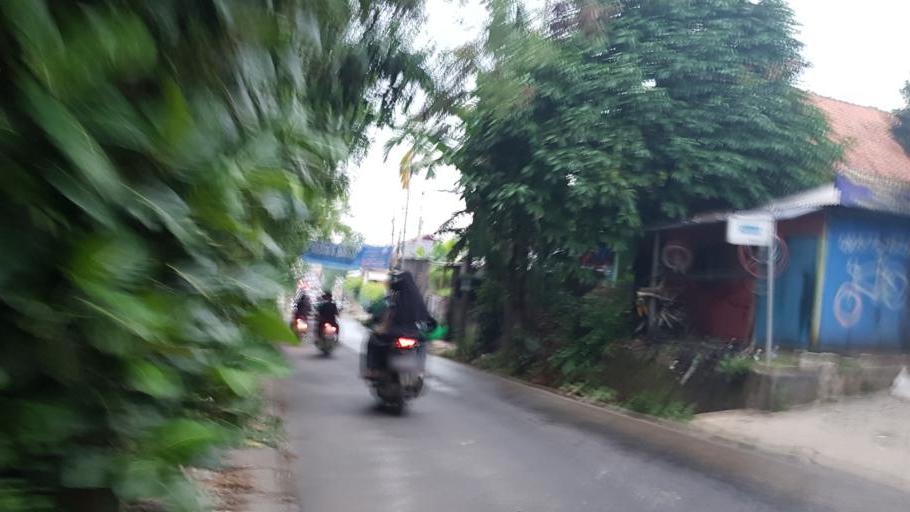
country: ID
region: West Java
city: Depok
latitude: -6.3671
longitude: 106.7972
